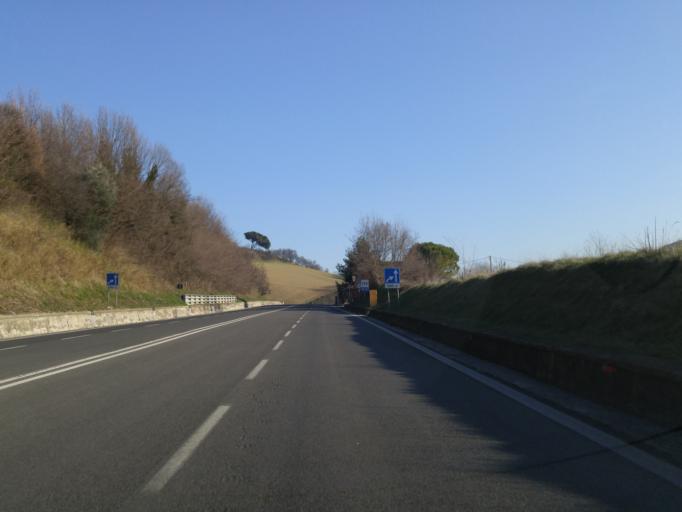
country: IT
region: The Marches
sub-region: Provincia di Pesaro e Urbino
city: Gradara
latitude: 43.9469
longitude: 12.8156
